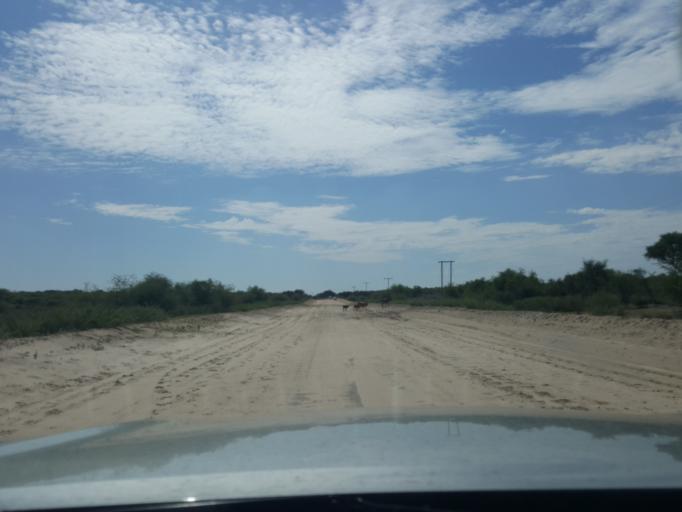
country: BW
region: Kweneng
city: Letlhakeng
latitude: -24.0507
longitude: 25.0243
